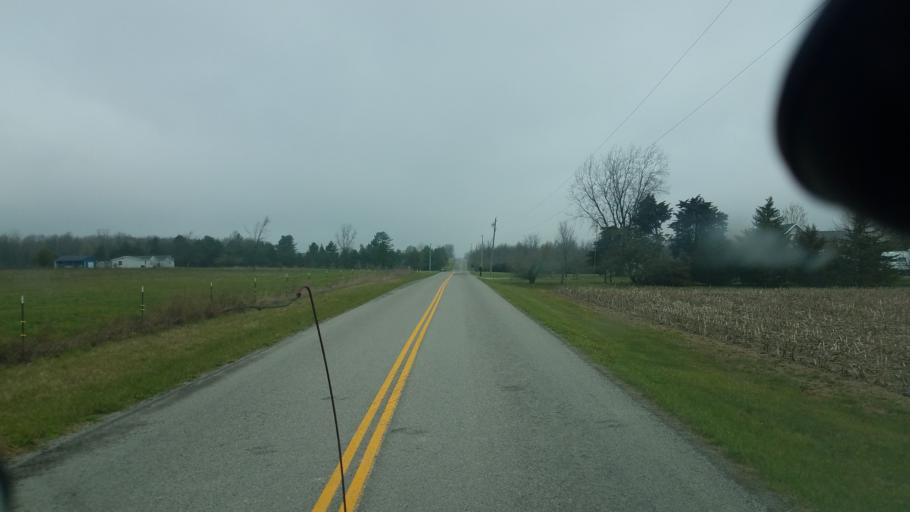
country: US
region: Ohio
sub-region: Logan County
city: Northwood
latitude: 40.4818
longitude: -83.6737
